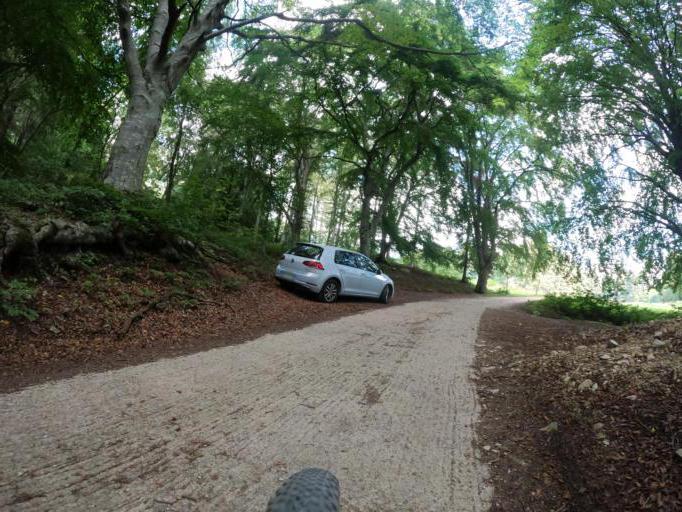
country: IT
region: Veneto
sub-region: Provincia di Verona
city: Ferrara di Monte Baldo
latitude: 45.6577
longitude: 10.8295
